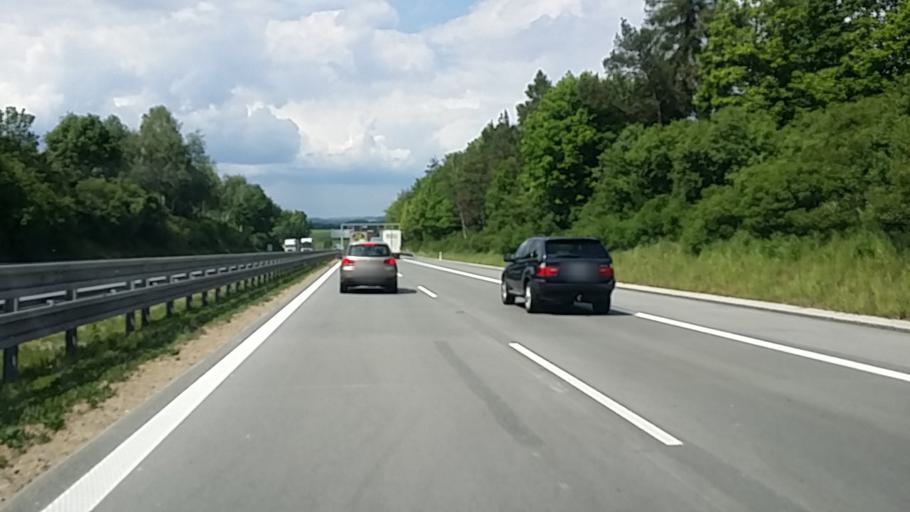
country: CZ
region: Central Bohemia
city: Trhovy Stepanov
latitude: 49.7350
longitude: 15.0421
